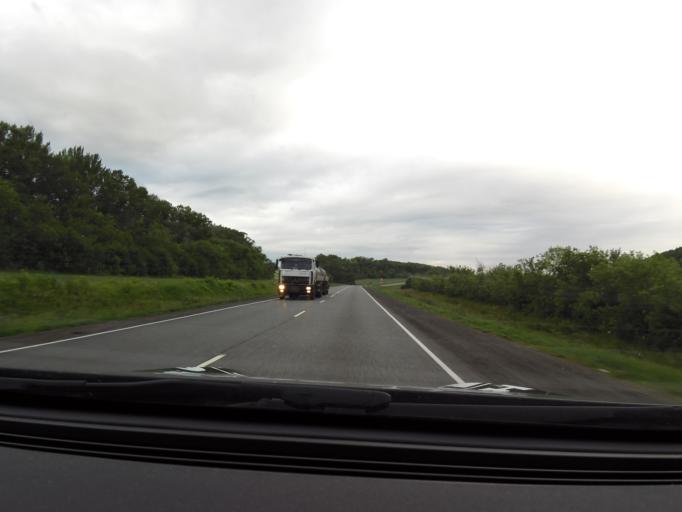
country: RU
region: Chuvashia
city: Kozlovka
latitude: 55.7834
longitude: 48.1791
